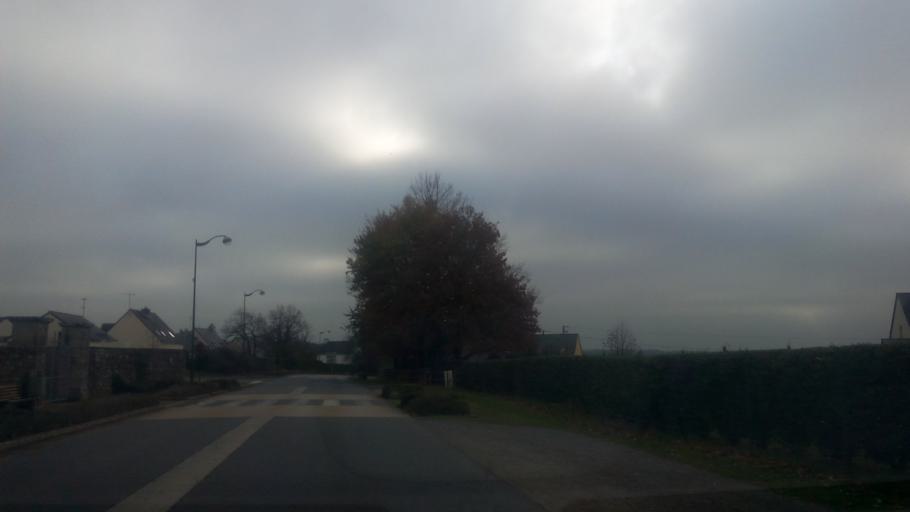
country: FR
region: Brittany
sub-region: Departement du Morbihan
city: Saint-Vincent-sur-Oust
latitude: 47.6971
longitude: -2.1455
